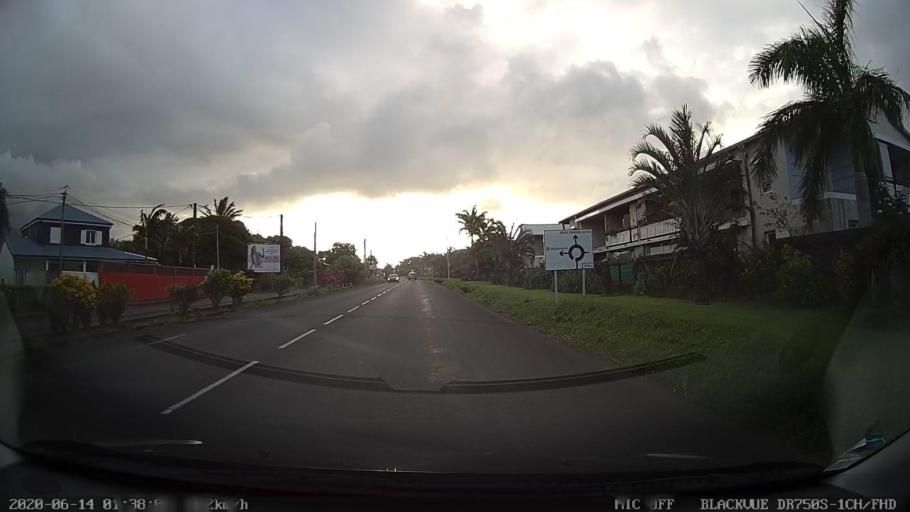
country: RE
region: Reunion
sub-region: Reunion
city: Bras-Panon
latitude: -21.0018
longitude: 55.6899
